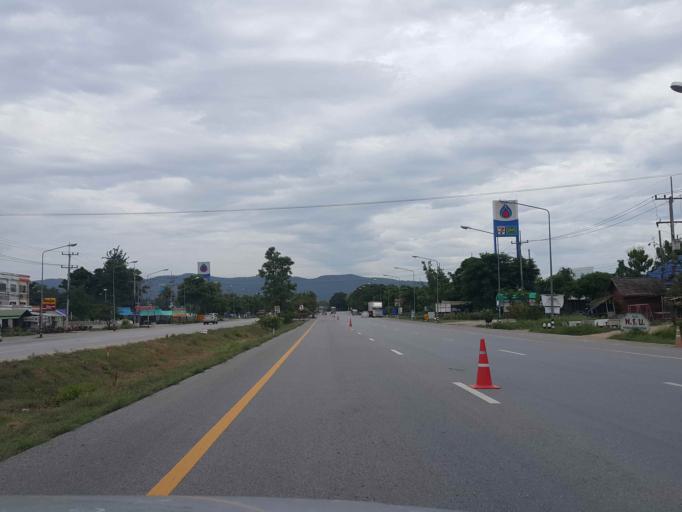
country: TH
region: Lampang
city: Thoen
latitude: 17.6176
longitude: 99.2328
